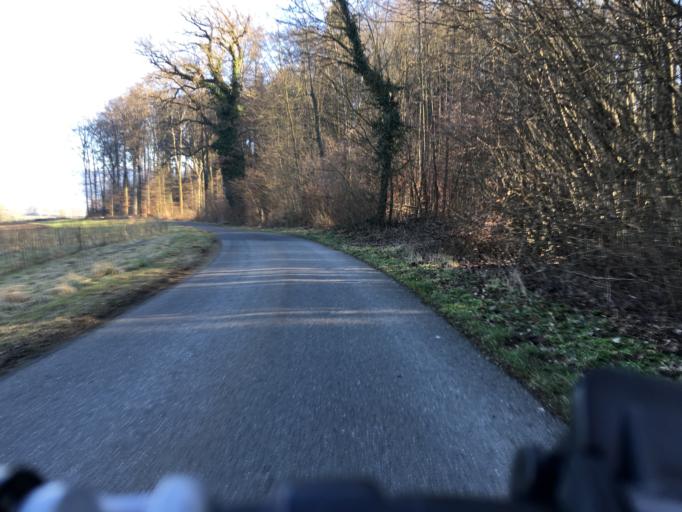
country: CH
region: Schaffhausen
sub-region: Bezirk Stein
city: Ramsen
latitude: 47.7224
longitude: 8.8038
